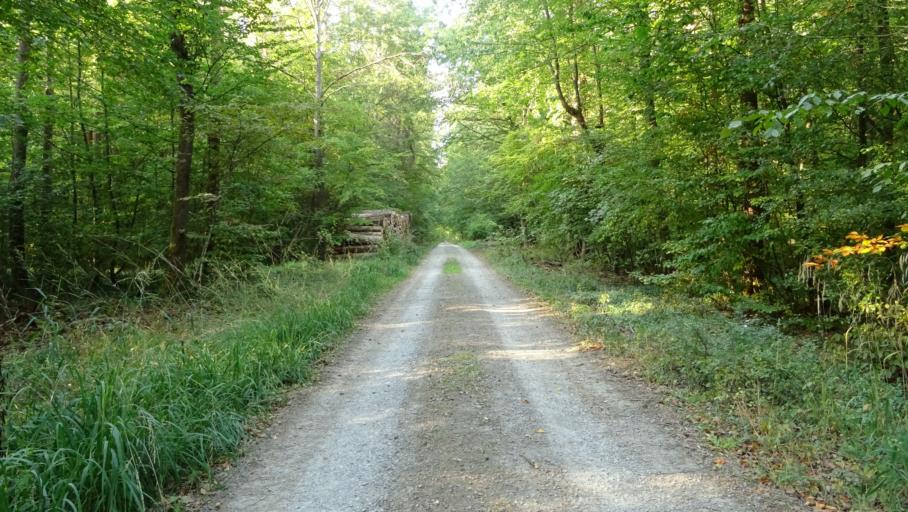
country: DE
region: Baden-Wuerttemberg
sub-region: Karlsruhe Region
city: Fahrenbach
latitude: 49.3981
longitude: 9.1663
